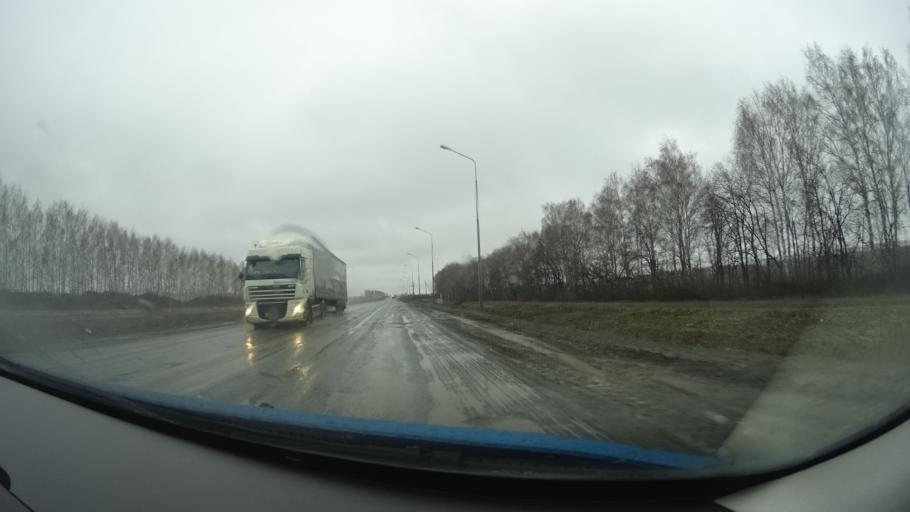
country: RU
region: Bashkortostan
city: Buzdyak
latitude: 54.6447
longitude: 54.5482
